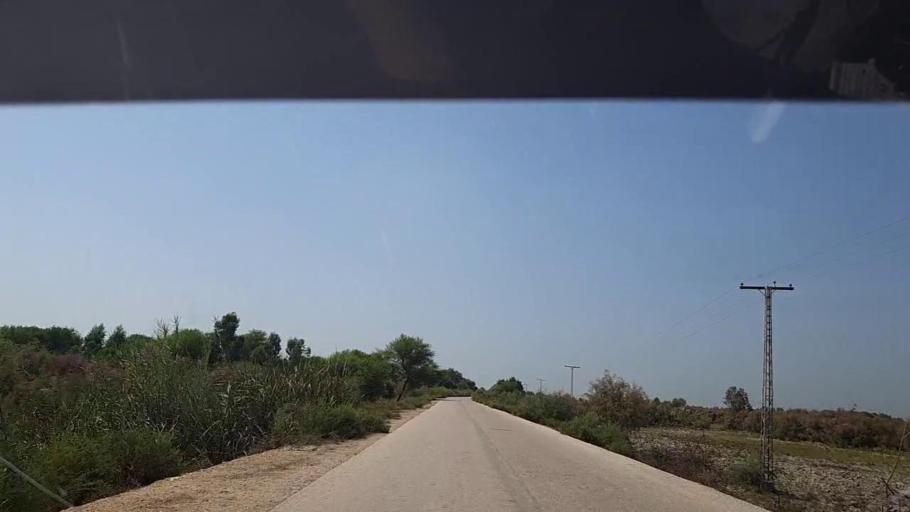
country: PK
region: Sindh
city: Ghauspur
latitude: 28.1535
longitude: 69.1605
